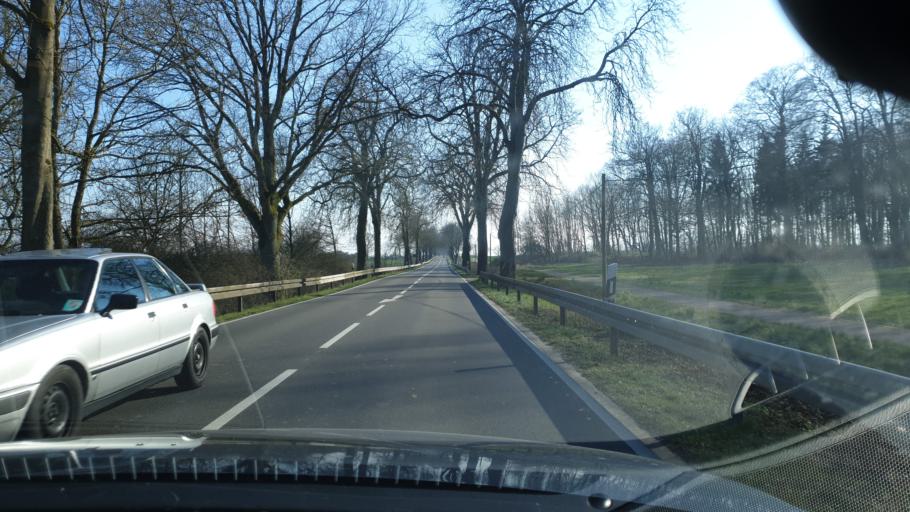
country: DE
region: Mecklenburg-Vorpommern
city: Lubstorf
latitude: 53.7152
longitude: 11.3990
